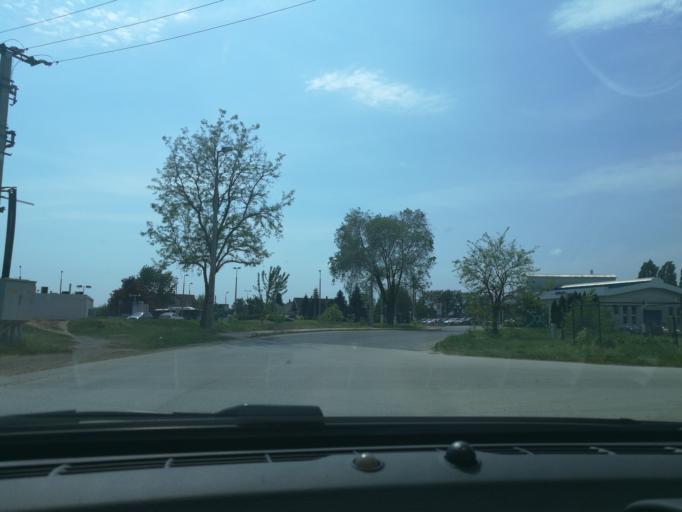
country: HU
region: Szabolcs-Szatmar-Bereg
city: Nyiregyhaza
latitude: 47.9583
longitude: 21.6850
